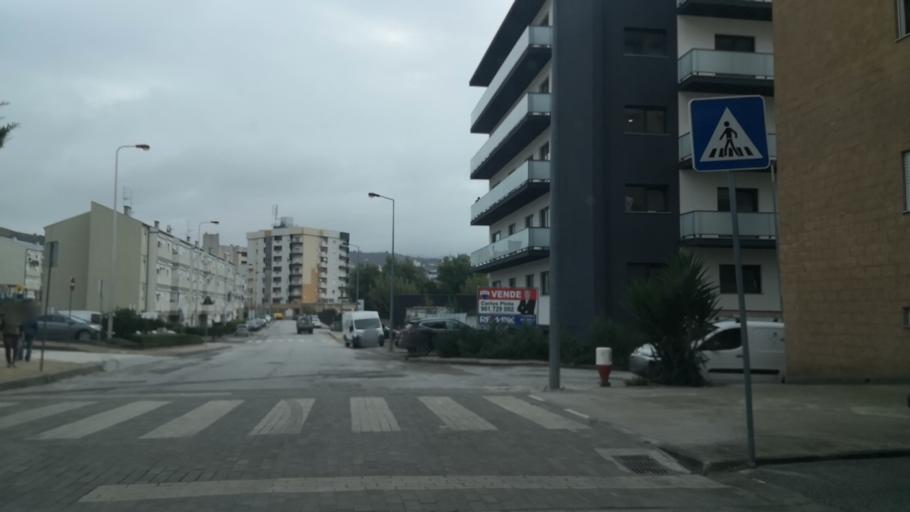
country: PT
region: Vila Real
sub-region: Peso da Regua
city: Godim
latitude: 41.1673
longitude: -7.8010
